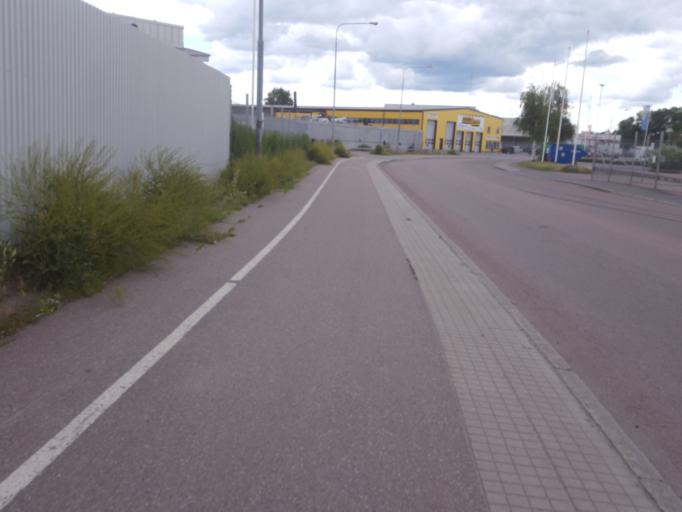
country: SE
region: Uppsala
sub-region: Uppsala Kommun
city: Uppsala
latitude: 59.8486
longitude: 17.6698
